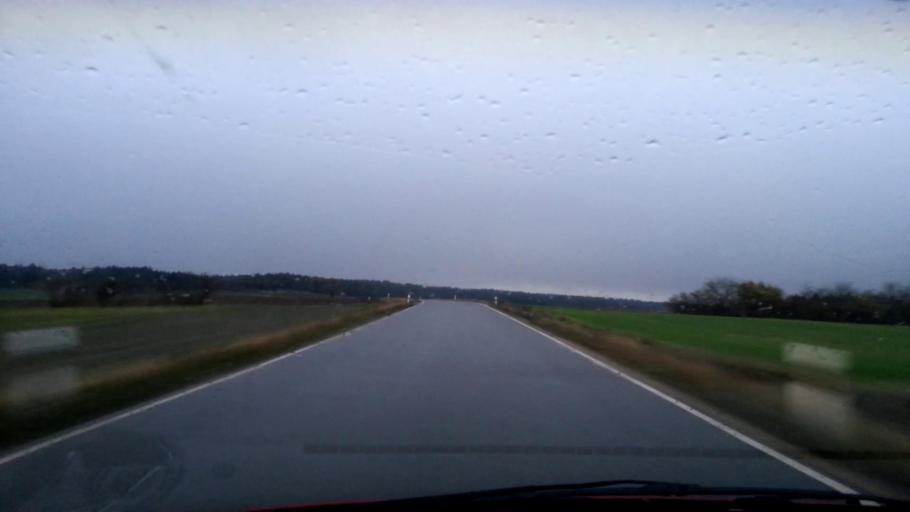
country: DE
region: Bavaria
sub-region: Upper Franconia
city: Konigsfeld
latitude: 49.9495
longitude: 11.1570
